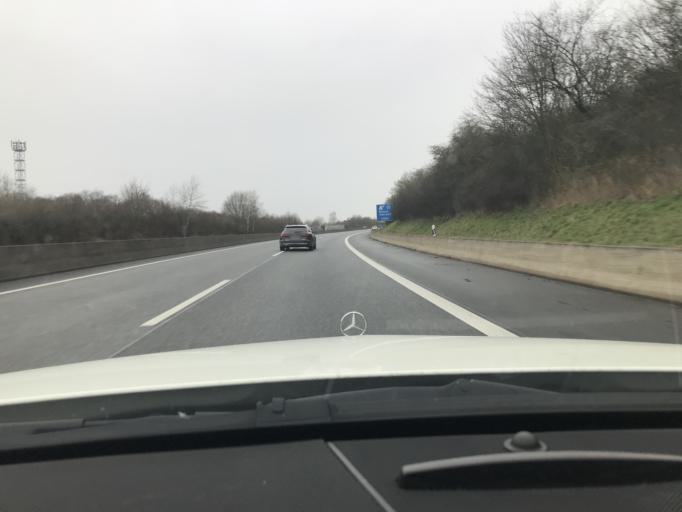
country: DE
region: Thuringia
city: Dankmarshausen
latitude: 50.9570
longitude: 10.0332
